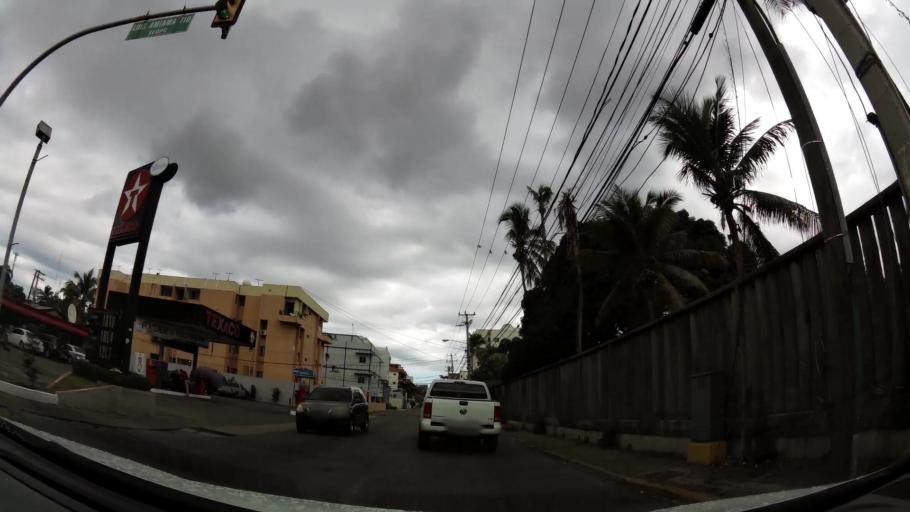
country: DO
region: Nacional
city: La Agustina
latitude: 18.4916
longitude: -69.9349
